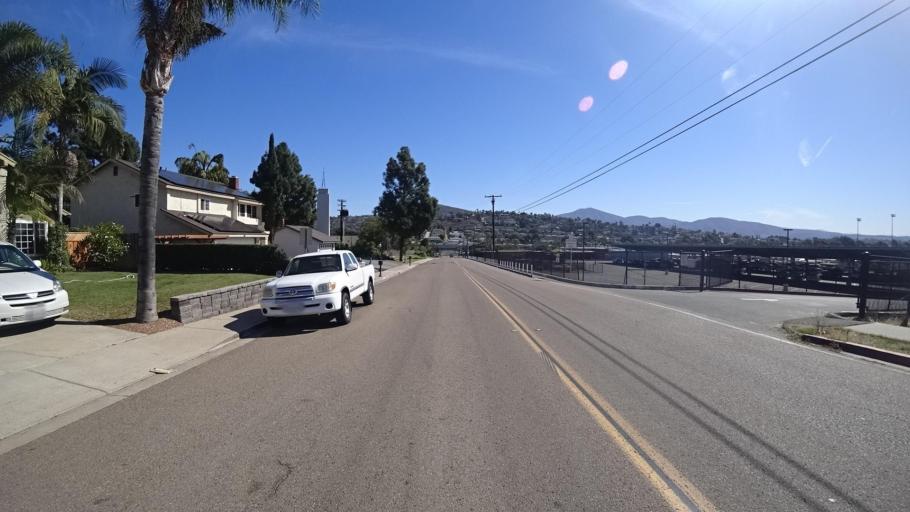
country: US
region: California
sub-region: San Diego County
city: Lemon Grove
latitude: 32.7250
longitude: -117.0188
